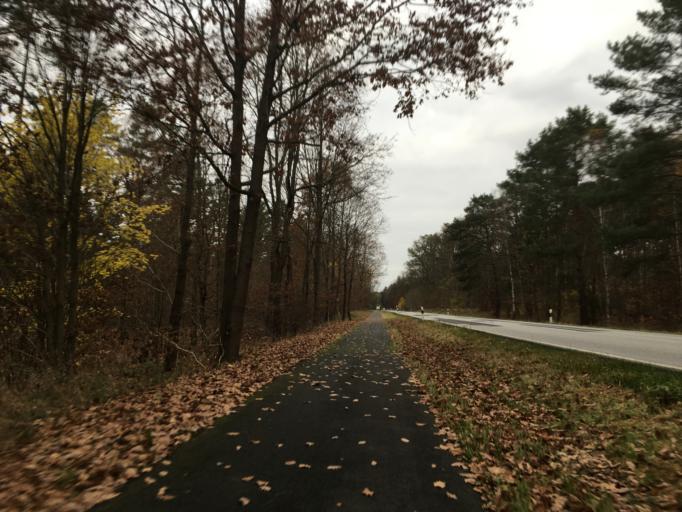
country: DE
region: Brandenburg
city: Mullrose
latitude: 52.2127
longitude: 14.4510
